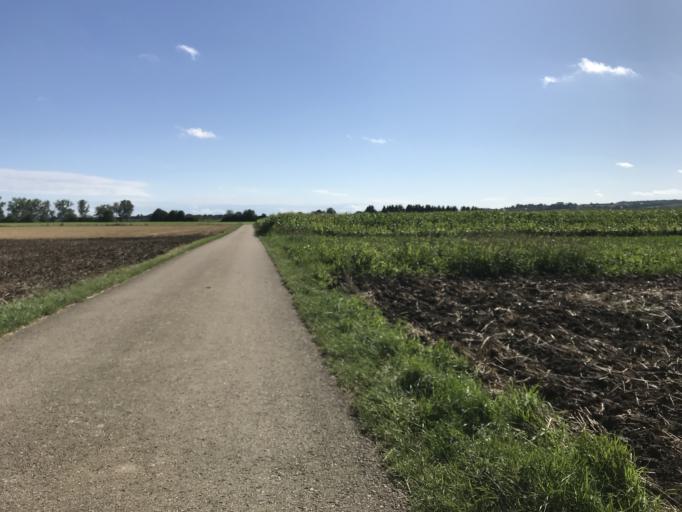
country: DE
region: Baden-Wuerttemberg
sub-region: Tuebingen Region
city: Langenau
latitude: 48.4766
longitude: 10.1216
